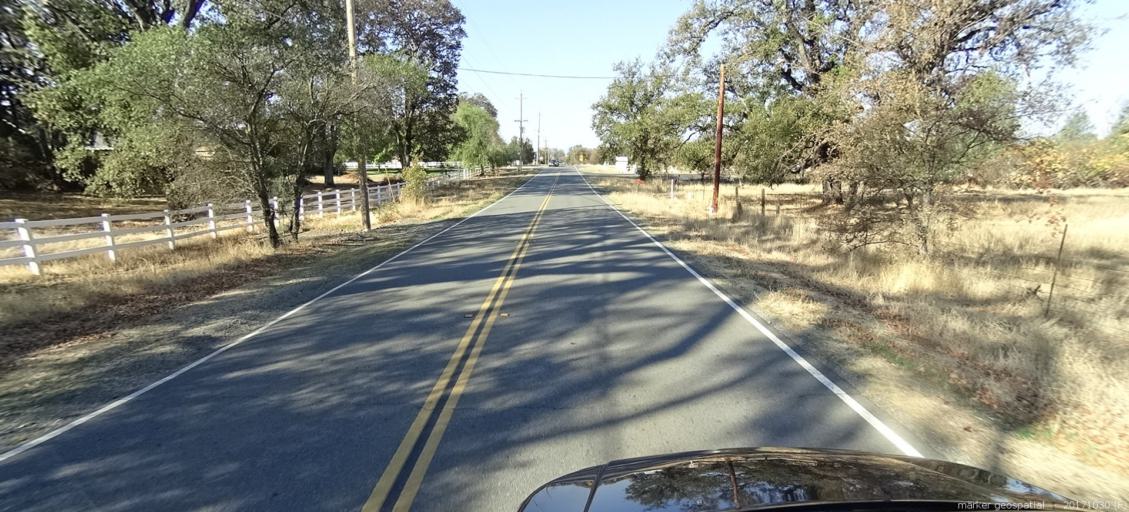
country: US
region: California
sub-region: Shasta County
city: Palo Cedro
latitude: 40.5638
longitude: -122.2309
